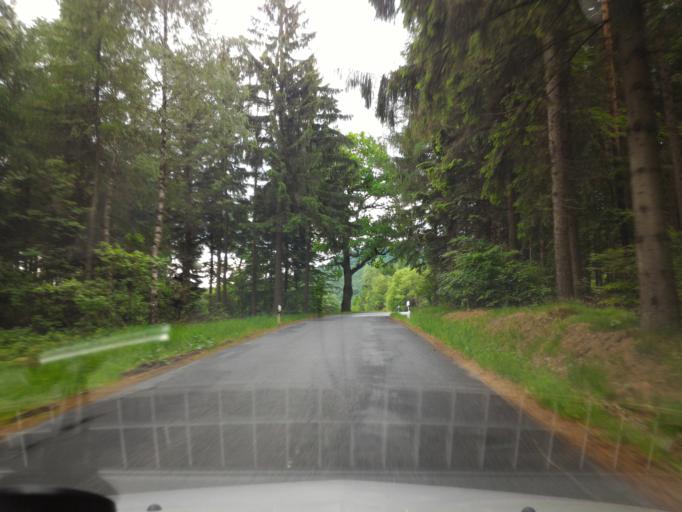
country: DE
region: Saxony
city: Kurort Oybin
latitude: 50.8388
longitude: 14.7213
